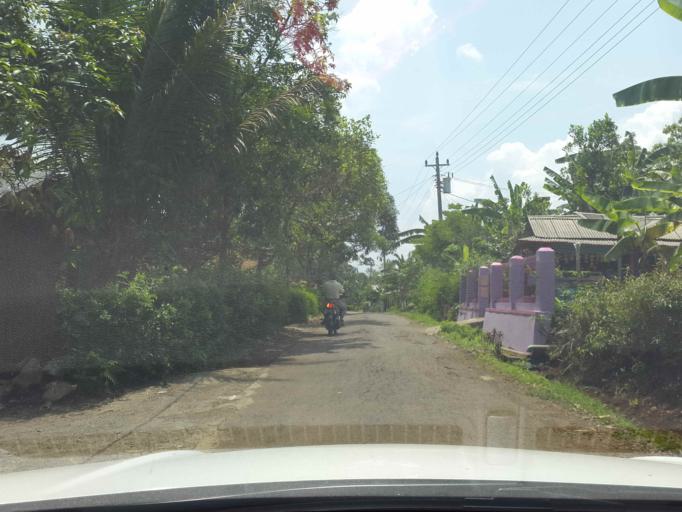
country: ID
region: Central Java
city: Bakung
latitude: -7.3446
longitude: 108.6786
